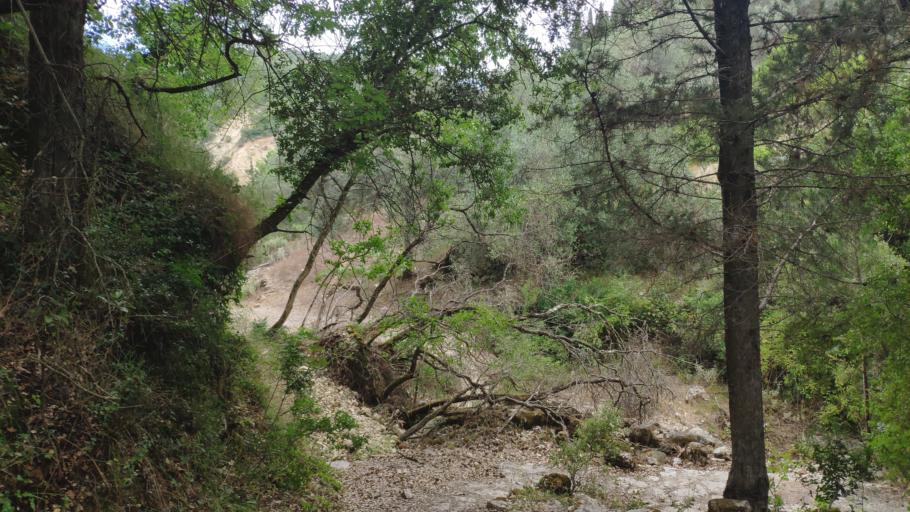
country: GR
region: Ionian Islands
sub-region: Lefkada
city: Lefkada
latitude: 38.8032
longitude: 20.6723
